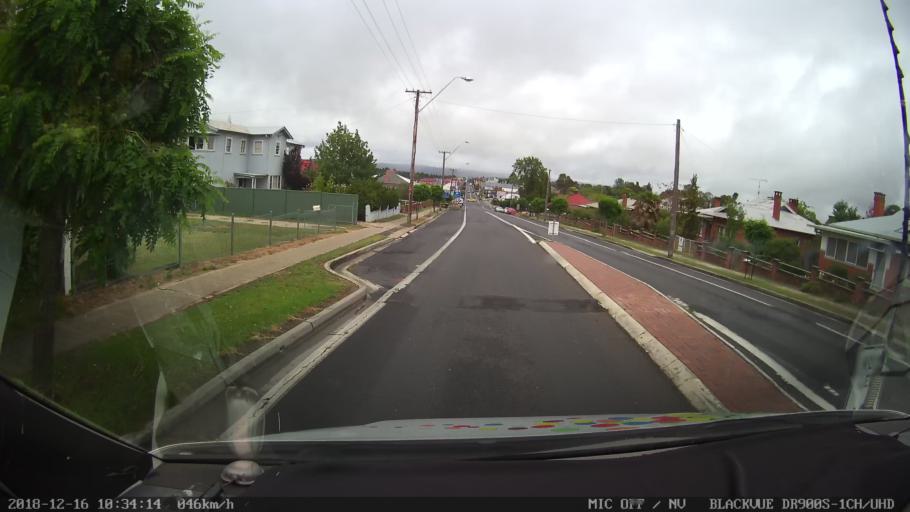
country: AU
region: New South Wales
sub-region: Tenterfield Municipality
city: Carrolls Creek
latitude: -29.0593
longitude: 152.0180
